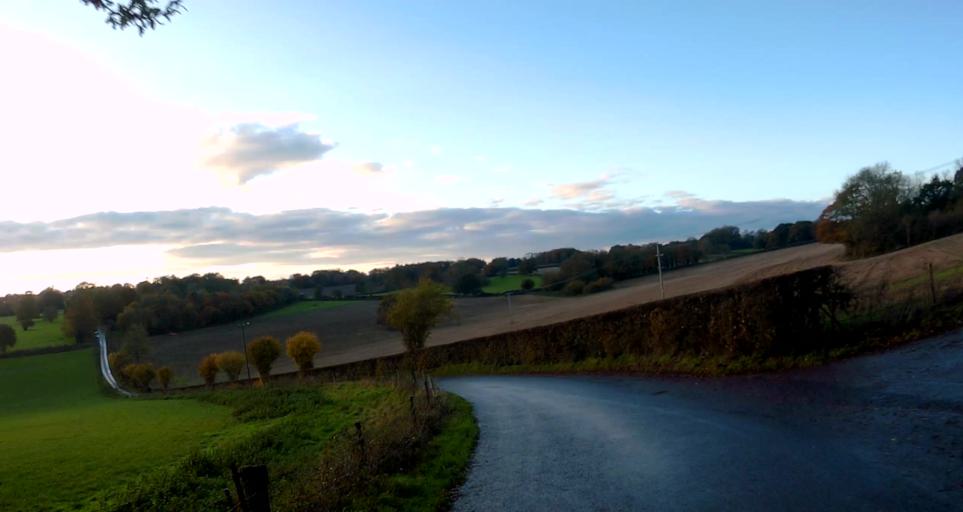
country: GB
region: England
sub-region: Hampshire
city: Basingstoke
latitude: 51.2159
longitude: -1.1022
